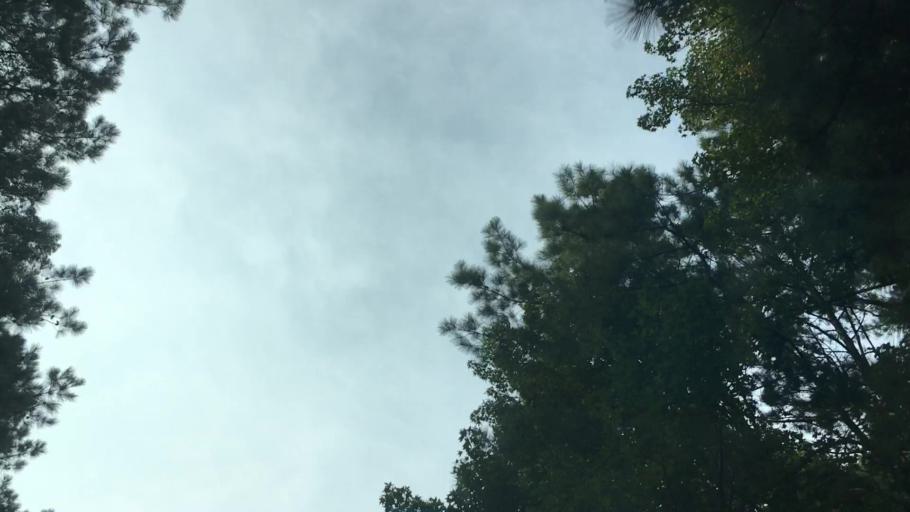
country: US
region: Alabama
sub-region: Bibb County
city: Woodstock
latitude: 33.2329
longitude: -87.1433
